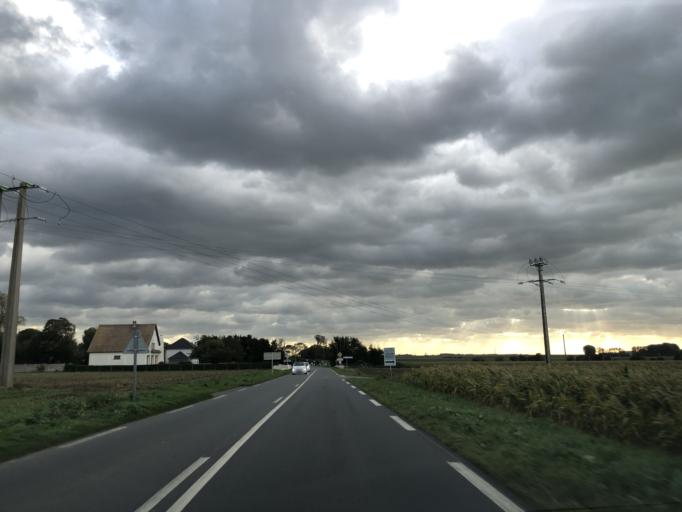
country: FR
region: Picardie
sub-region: Departement de la Somme
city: Ault
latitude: 50.0804
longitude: 1.4396
